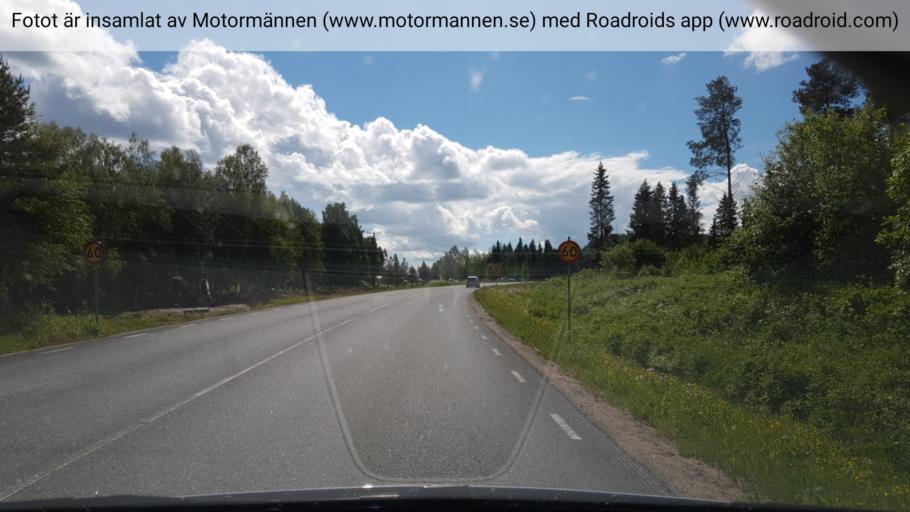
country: SE
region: Norrbotten
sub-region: Overtornea Kommun
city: OEvertornea
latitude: 66.3905
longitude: 23.6380
